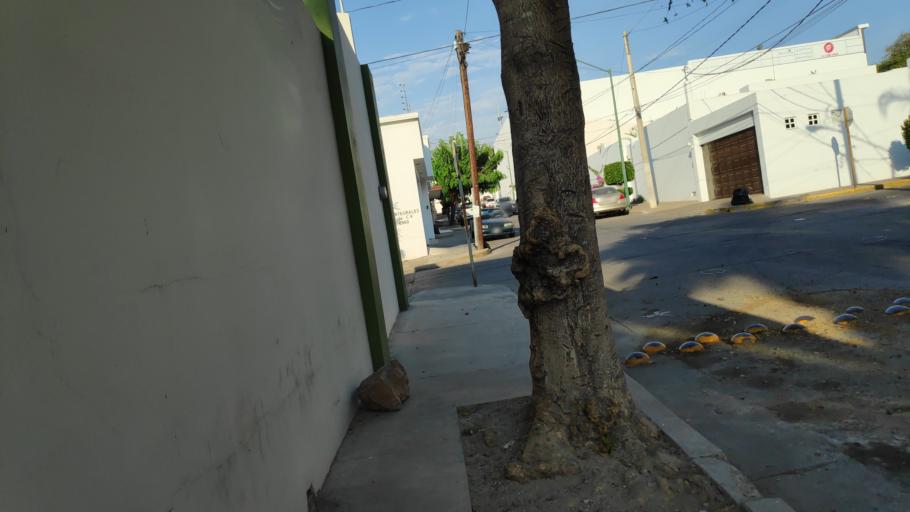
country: MX
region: Sinaloa
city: Culiacan
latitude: 24.7900
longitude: -107.3973
